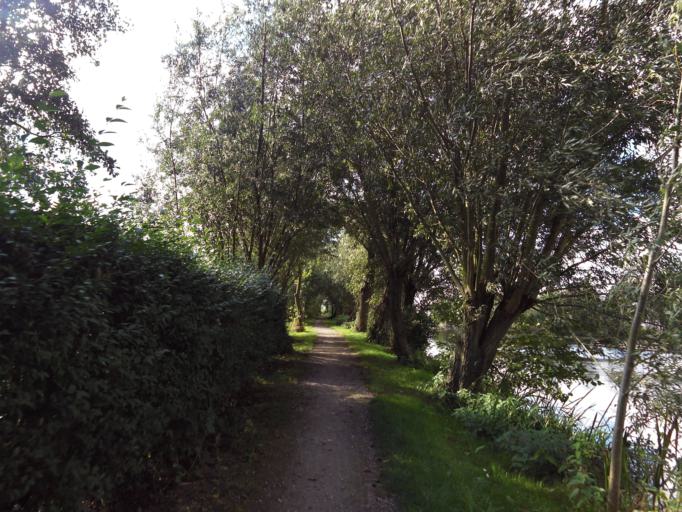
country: NL
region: South Holland
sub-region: Gemeente Boskoop
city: Boskoop
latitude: 52.1019
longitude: 4.6163
